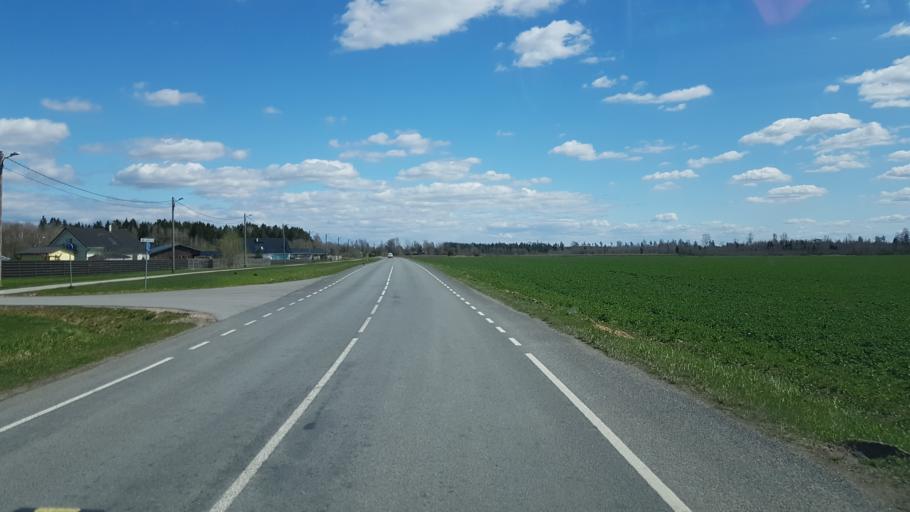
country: EE
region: Viljandimaa
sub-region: Viiratsi vald
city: Viiratsi
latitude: 58.3592
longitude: 25.6491
